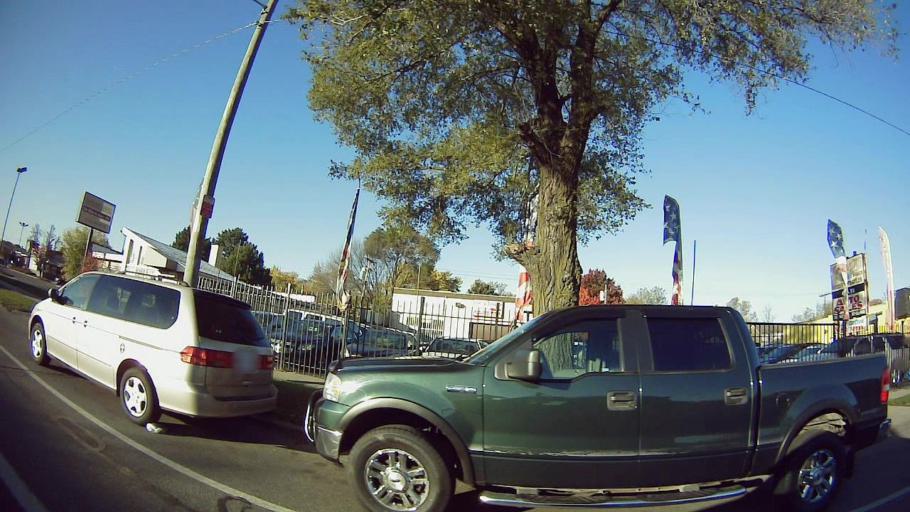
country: US
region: Michigan
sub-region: Macomb County
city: Warren
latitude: 42.4422
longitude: -83.0246
